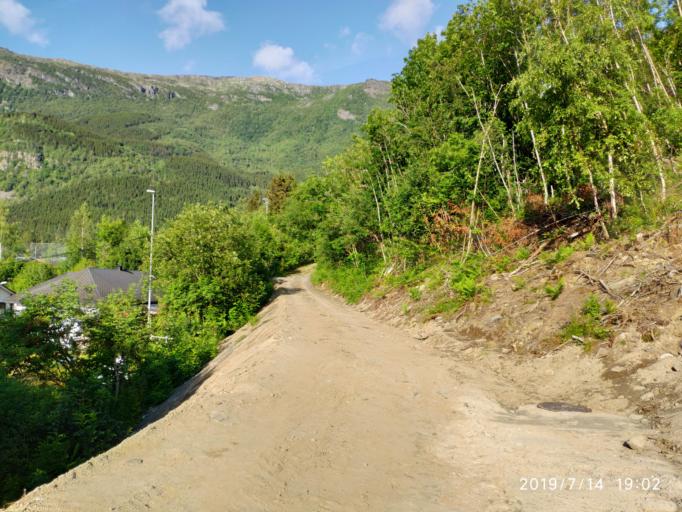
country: NO
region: Hordaland
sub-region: Ullensvang
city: Kinsarvik
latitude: 60.3178
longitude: 6.6583
